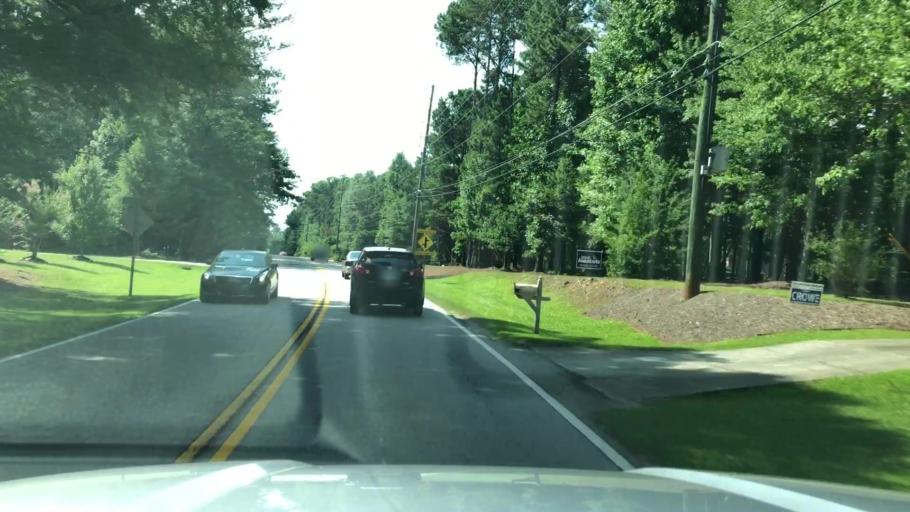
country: US
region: Georgia
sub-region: Paulding County
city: Dallas
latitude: 33.9669
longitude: -84.7926
